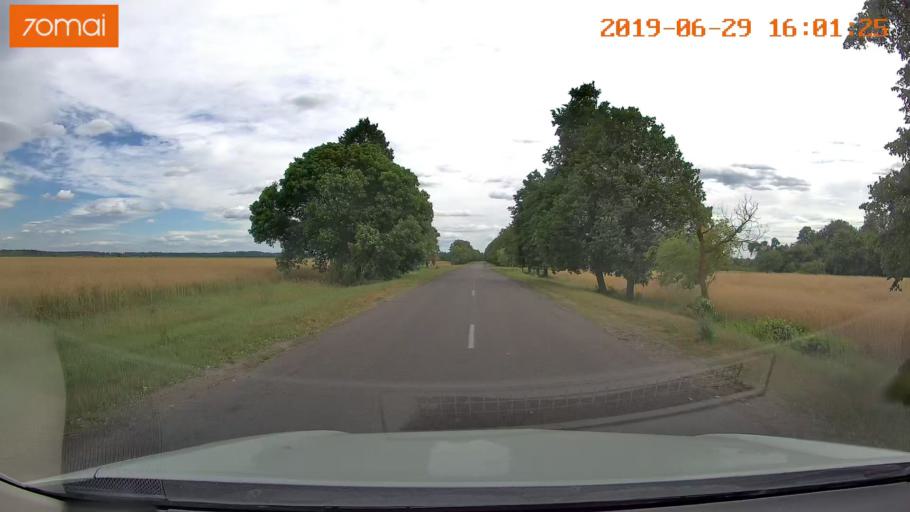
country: BY
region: Brest
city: Luninyets
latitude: 52.2476
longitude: 27.0166
